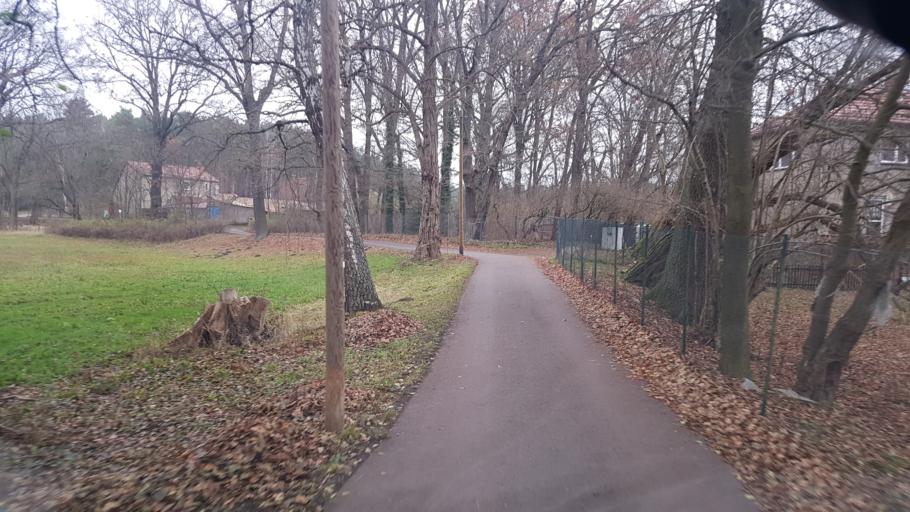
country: DE
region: Brandenburg
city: Schenkendobern
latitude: 51.9725
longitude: 14.6512
